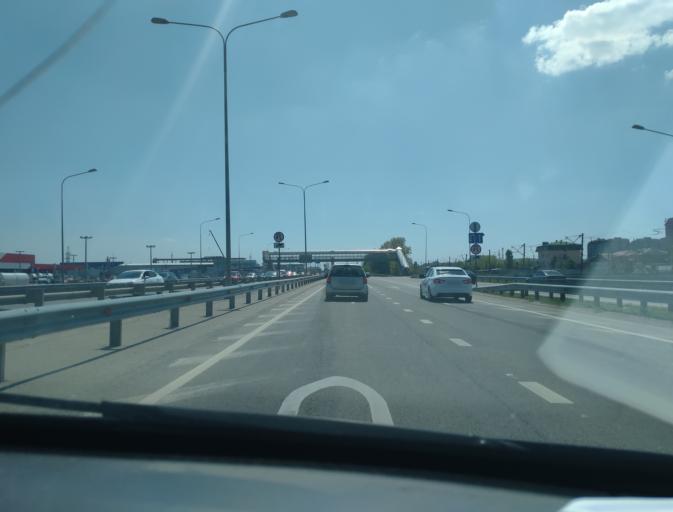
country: RU
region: Krasnodarskiy
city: Krasnodar
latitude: 45.0974
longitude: 38.9924
